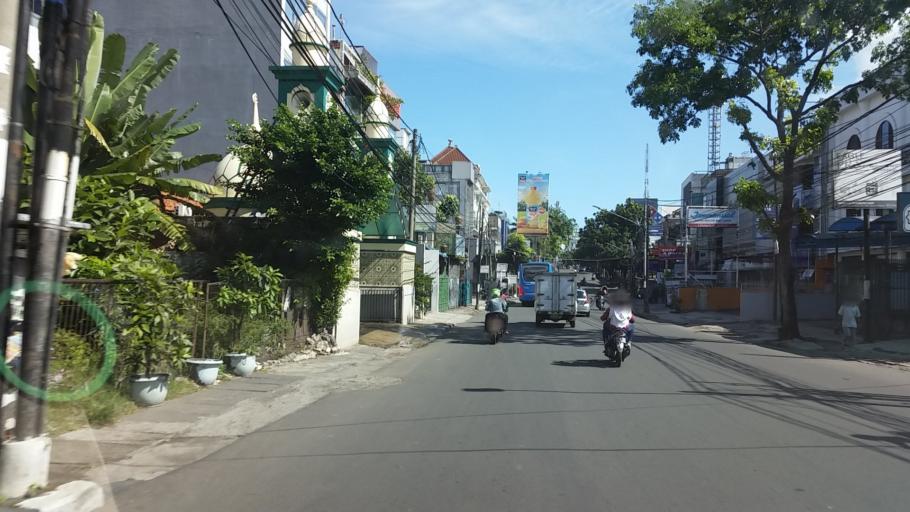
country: ID
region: Jakarta Raya
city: Jakarta
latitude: -6.2581
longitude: 106.7895
